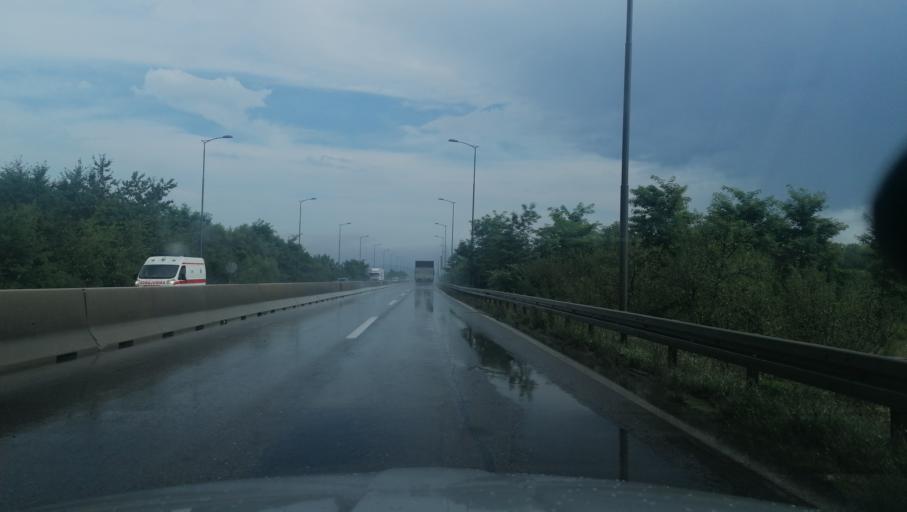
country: BA
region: Republika Srpska
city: Trn
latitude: 44.8327
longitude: 17.2130
